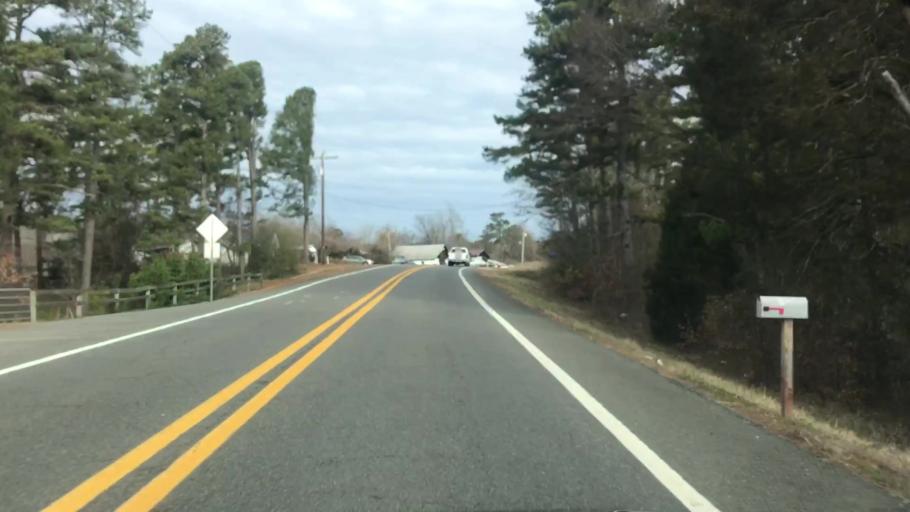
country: US
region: Arkansas
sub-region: Montgomery County
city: Mount Ida
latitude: 34.5839
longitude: -93.6630
